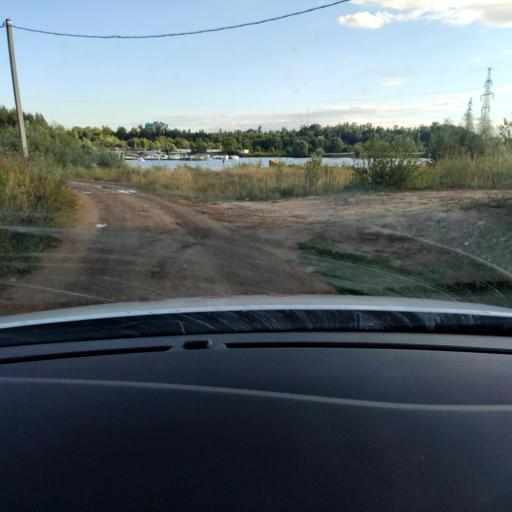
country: RU
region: Tatarstan
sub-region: Gorod Kazan'
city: Kazan
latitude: 55.8368
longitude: 49.1865
